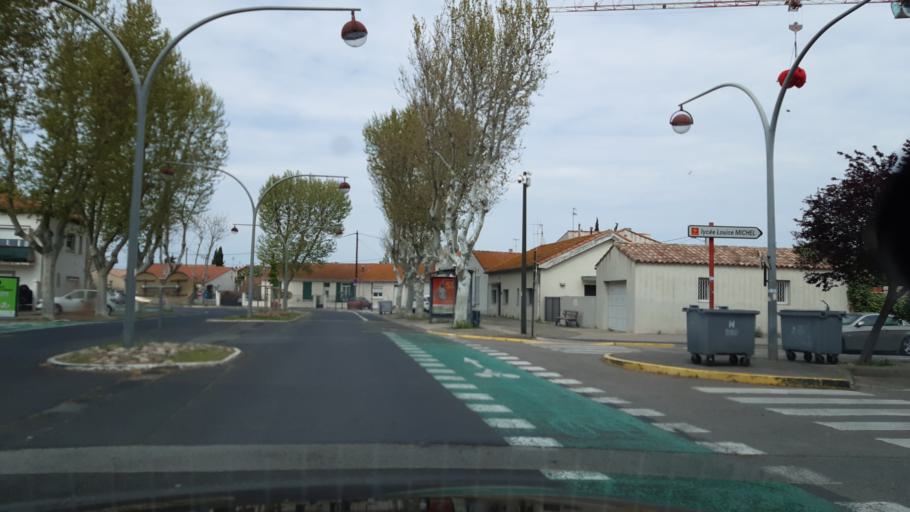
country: FR
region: Languedoc-Roussillon
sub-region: Departement de l'Aude
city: Narbonne
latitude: 43.1899
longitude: 3.0179
